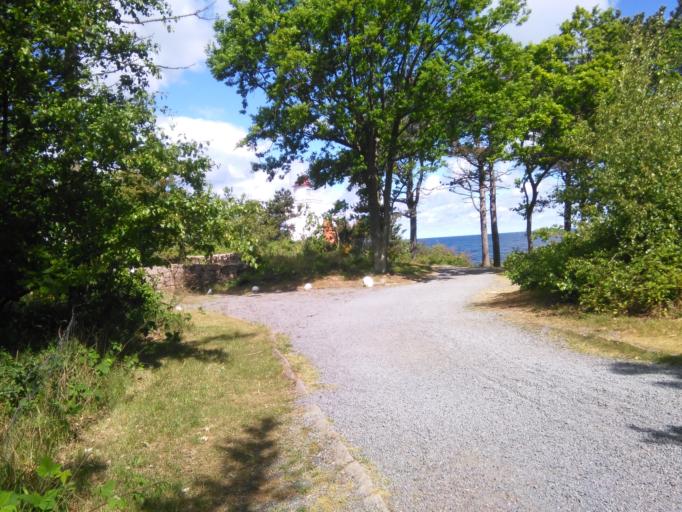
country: DK
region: Capital Region
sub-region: Bornholm Kommune
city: Ronne
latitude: 55.2976
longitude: 14.7744
